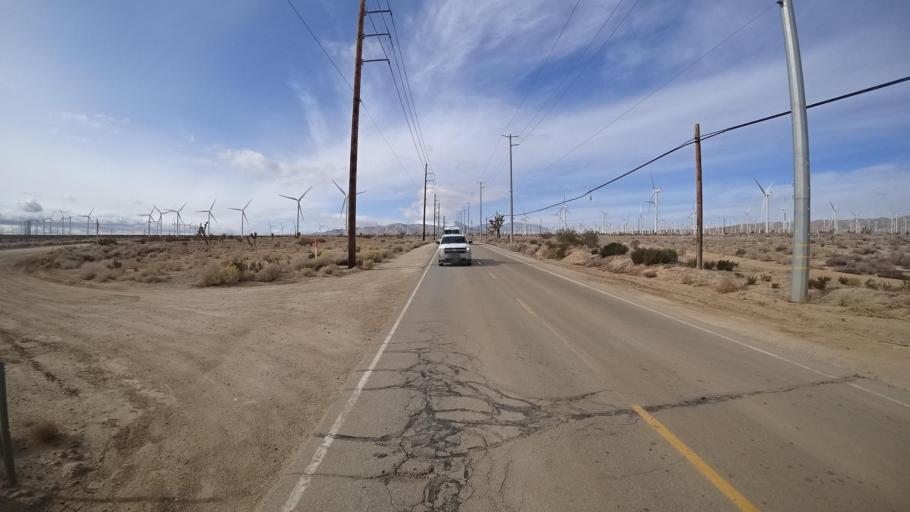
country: US
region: California
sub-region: Kern County
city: Mojave
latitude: 35.0397
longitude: -118.2474
